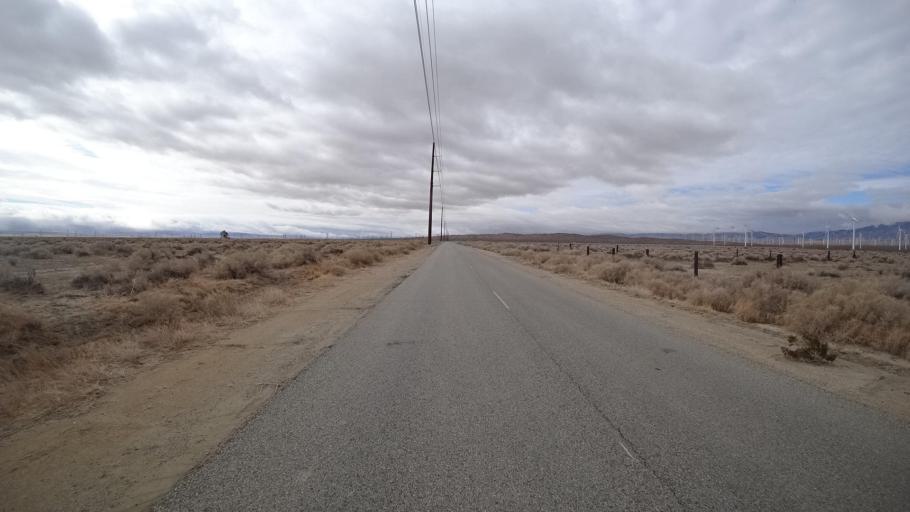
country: US
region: California
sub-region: Los Angeles County
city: Green Valley
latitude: 34.8626
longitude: -118.4079
